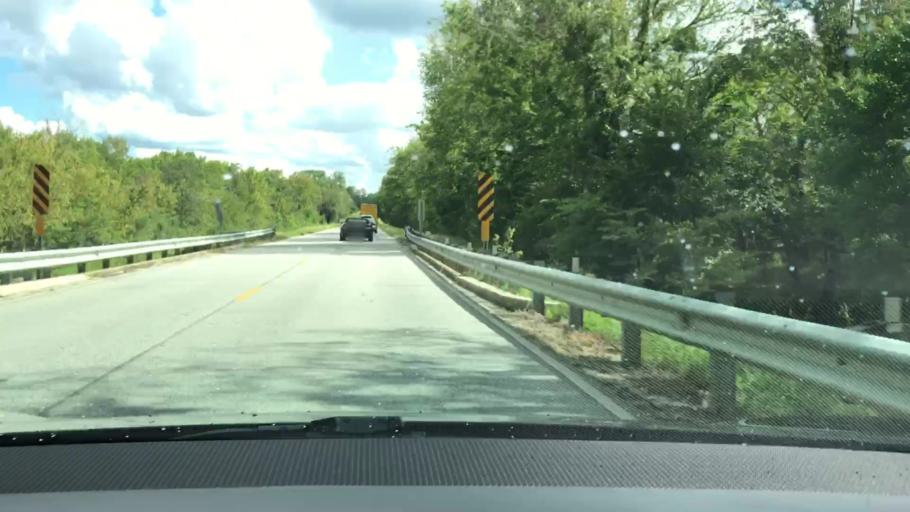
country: US
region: Alabama
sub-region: Montgomery County
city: Pike Road
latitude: 32.2222
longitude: -86.0911
